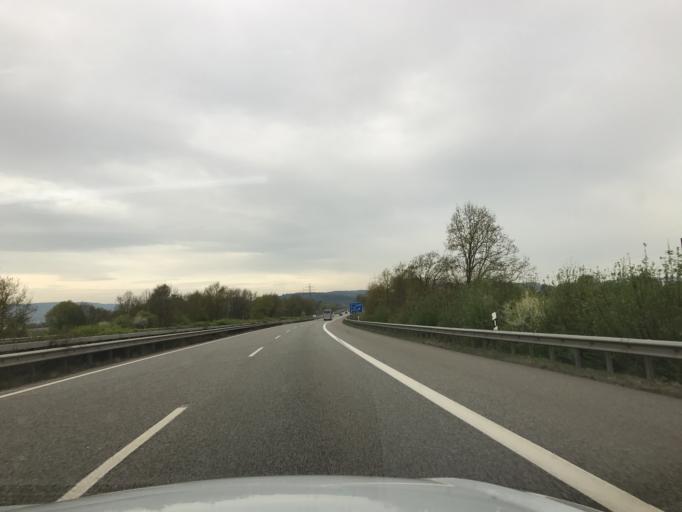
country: DE
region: Rheinland-Pfalz
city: Neuerburg
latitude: 49.9895
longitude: 6.9240
